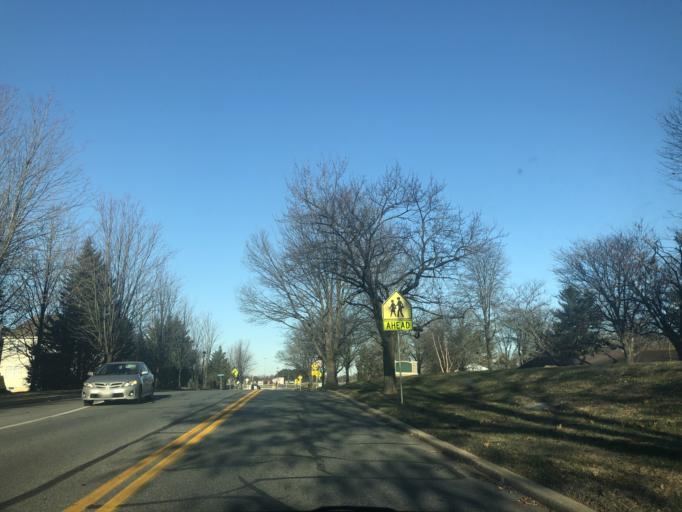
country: US
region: Maryland
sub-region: Howard County
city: Columbia
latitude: 39.2066
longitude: -76.8298
